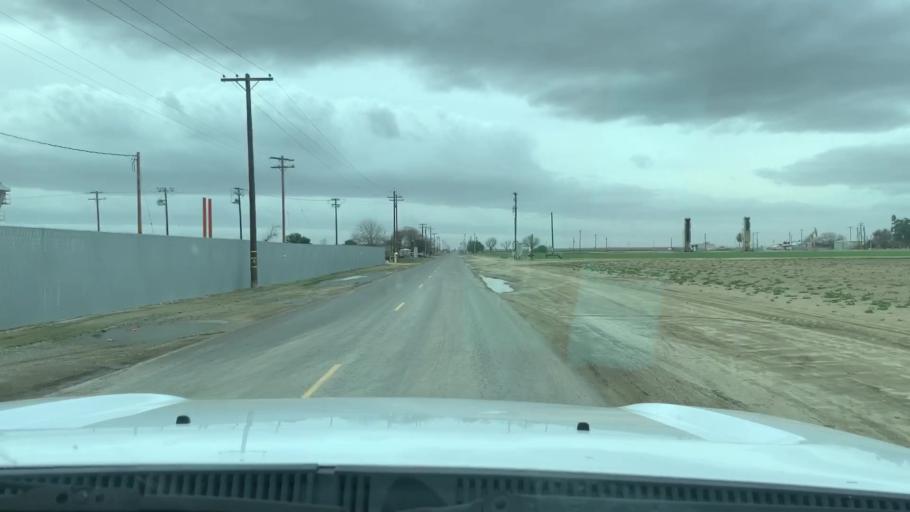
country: US
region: California
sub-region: Kern County
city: Shafter
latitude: 35.5292
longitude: -119.2722
